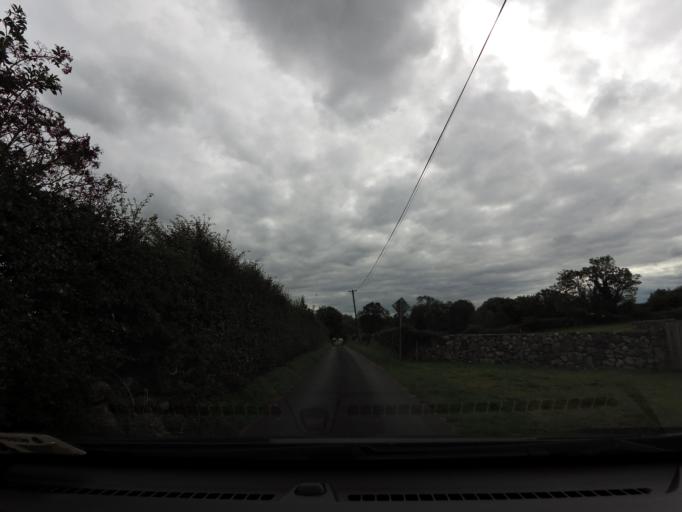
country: IE
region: Connaught
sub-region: County Galway
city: Loughrea
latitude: 53.1615
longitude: -8.4704
